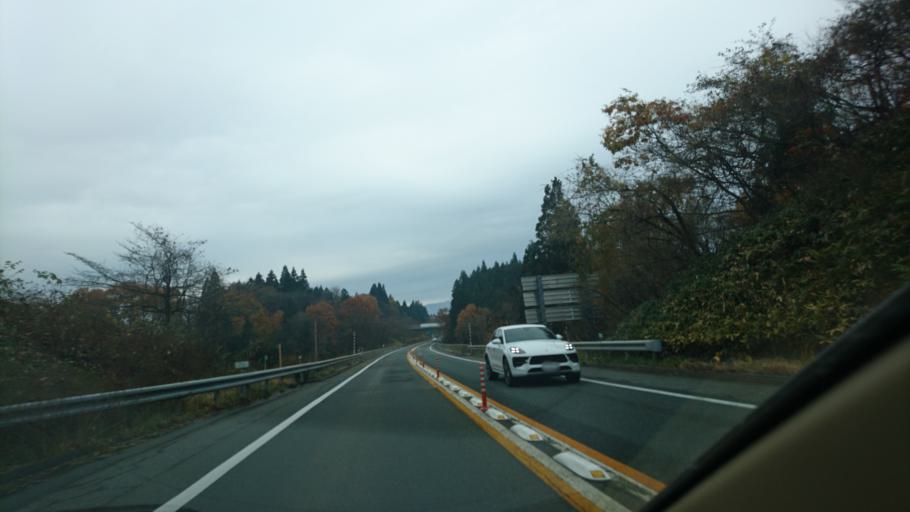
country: JP
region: Iwate
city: Kitakami
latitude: 39.2838
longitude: 140.9984
